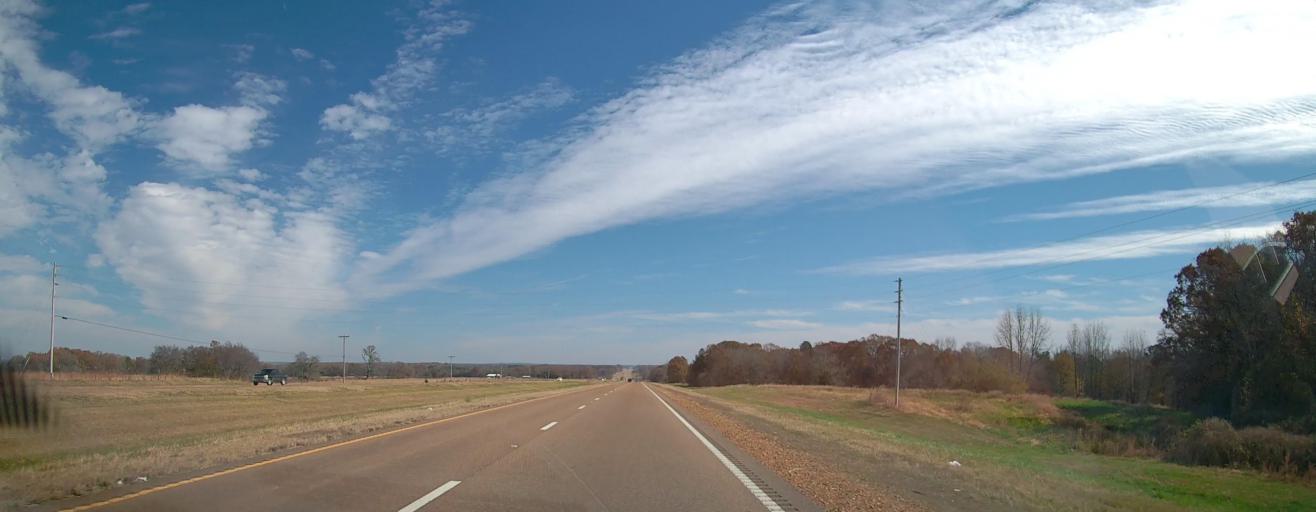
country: US
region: Mississippi
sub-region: Benton County
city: Ashland
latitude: 34.9461
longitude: -89.3167
